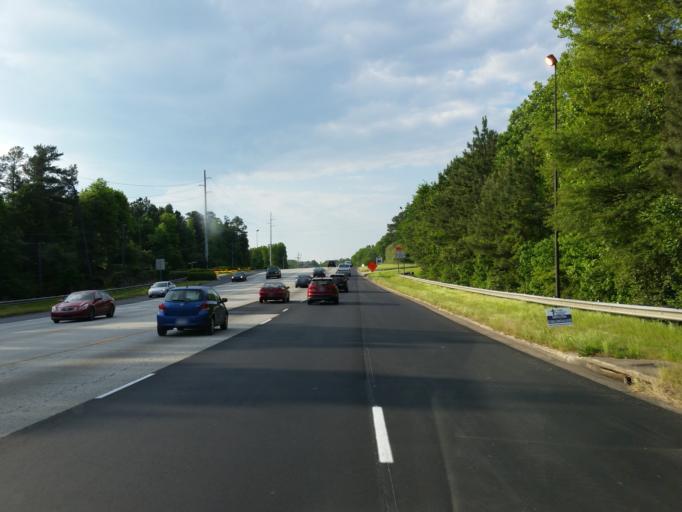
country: US
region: Georgia
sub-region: Cobb County
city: Vinings
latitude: 33.8320
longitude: -84.4928
